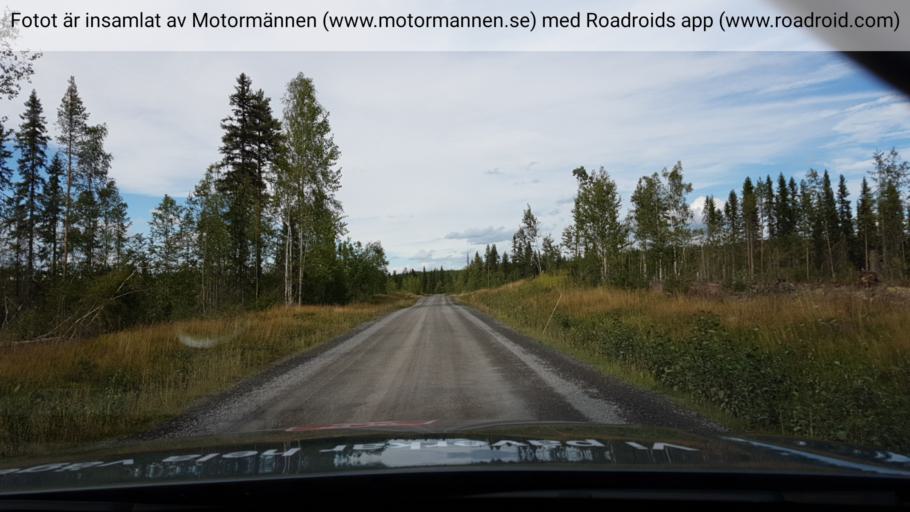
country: SE
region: Jaemtland
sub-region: Braecke Kommun
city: Braecke
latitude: 63.2637
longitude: 15.3777
